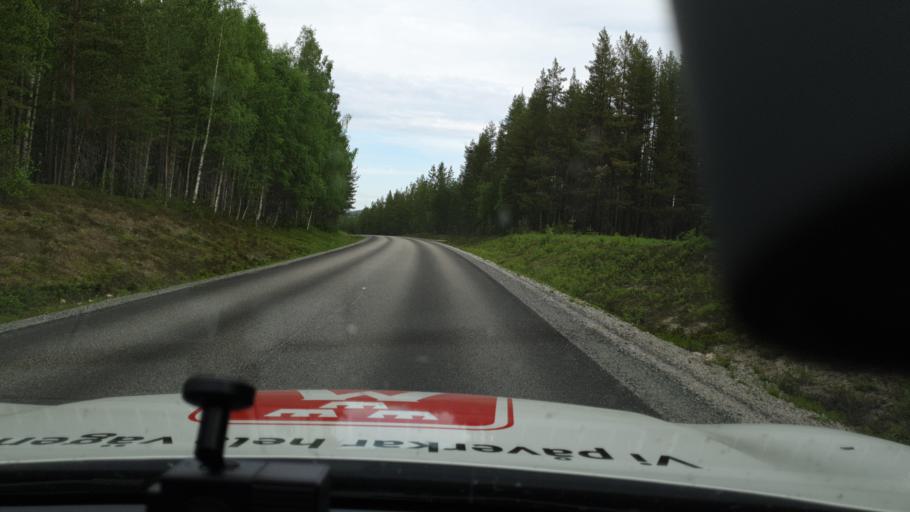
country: SE
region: Vaesterbotten
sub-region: Lycksele Kommun
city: Lycksele
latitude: 64.8854
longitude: 18.7327
